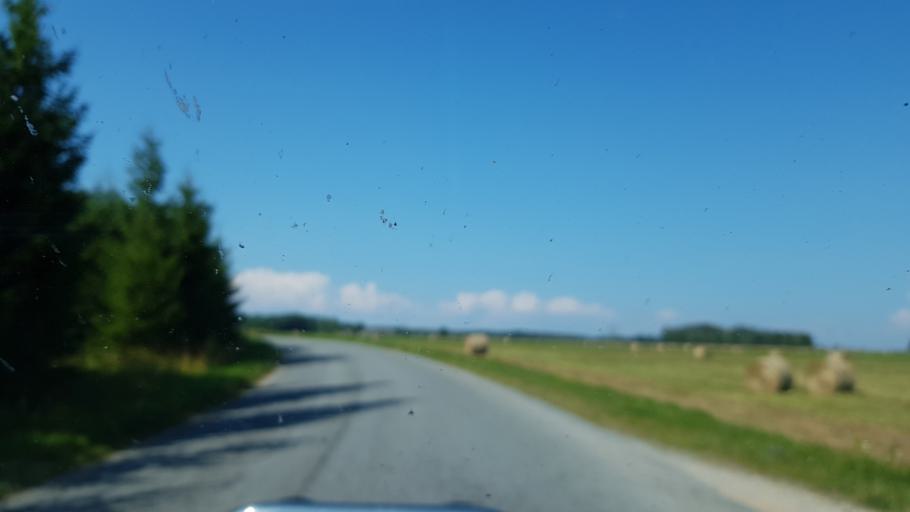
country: EE
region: Tartu
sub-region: Alatskivi vald
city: Kallaste
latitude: 58.6650
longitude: 27.0400
